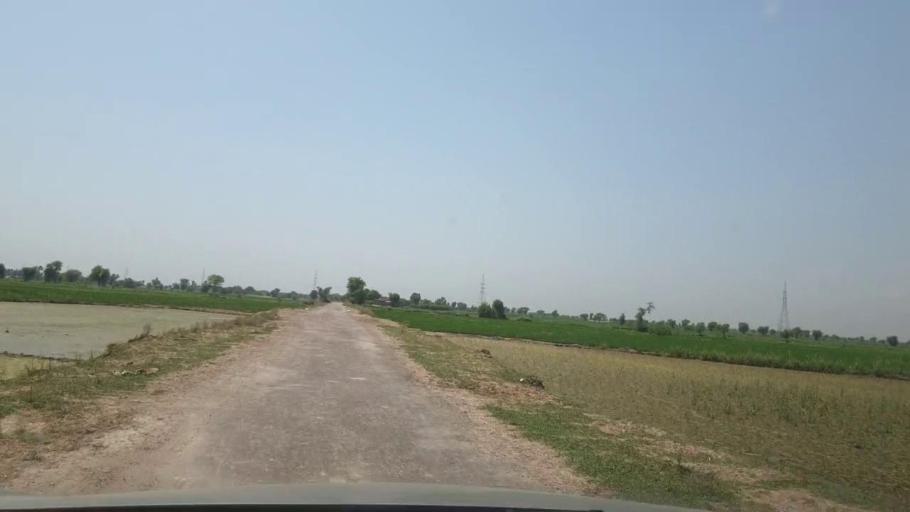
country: PK
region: Sindh
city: Warah
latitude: 27.4996
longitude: 67.7545
